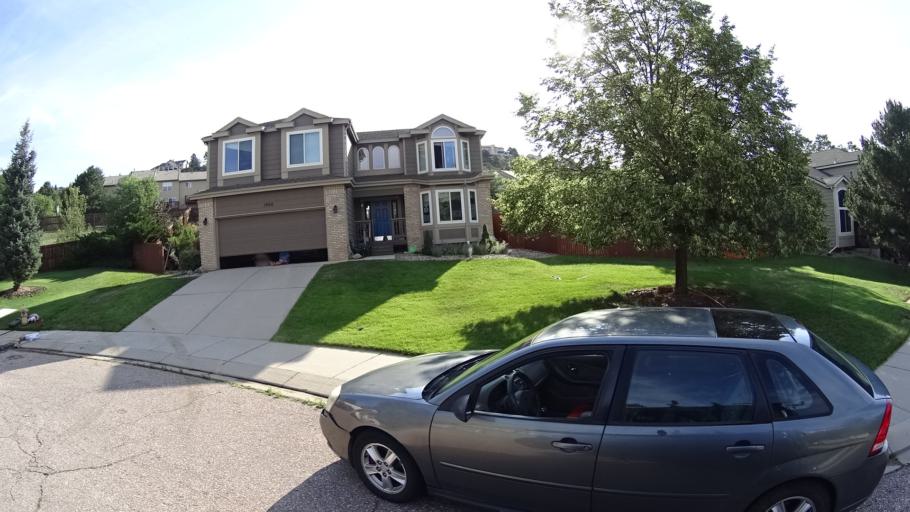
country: US
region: Colorado
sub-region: El Paso County
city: Air Force Academy
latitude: 38.9308
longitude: -104.8629
